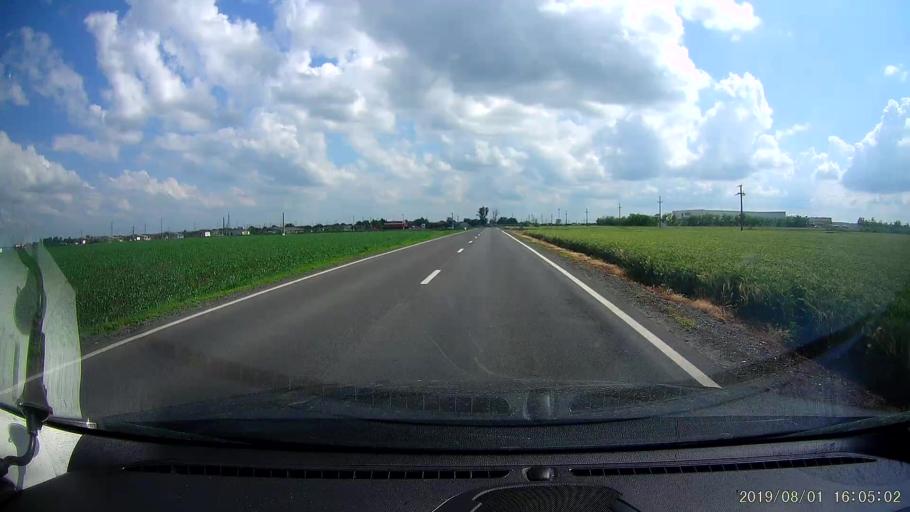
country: RO
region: Calarasi
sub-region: Comuna Dragalina
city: Drajna Noua
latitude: 44.4331
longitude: 27.3776
